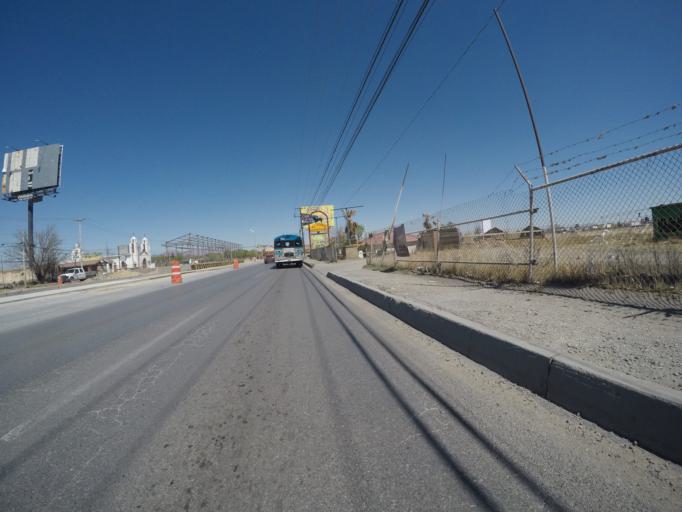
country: MX
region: Chihuahua
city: Ciudad Juarez
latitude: 31.6833
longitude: -106.4244
